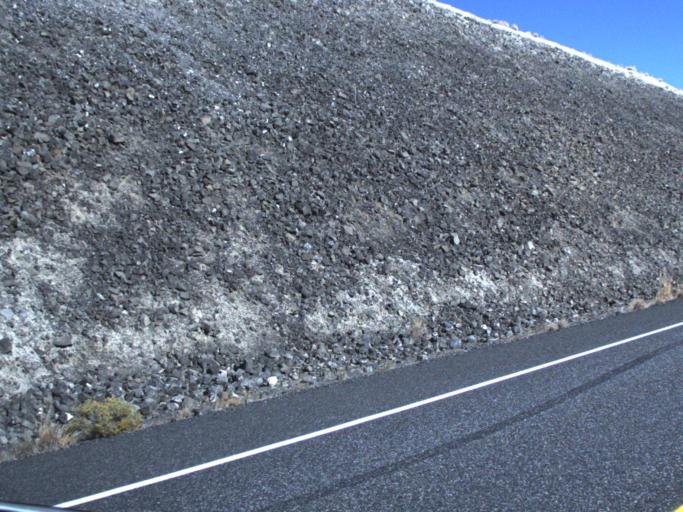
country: US
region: Washington
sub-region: Benton County
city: Highland
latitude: 46.1335
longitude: -119.0890
